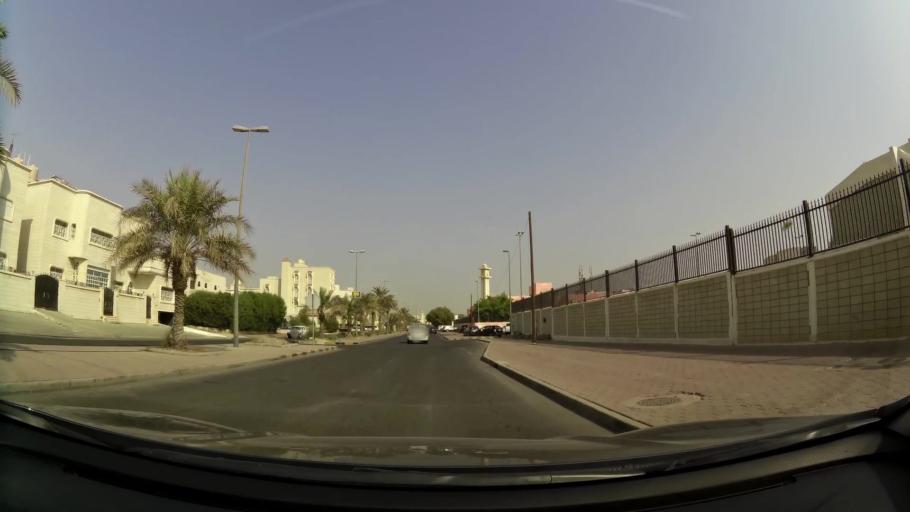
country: KW
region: Al Asimah
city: Ar Rabiyah
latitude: 29.2714
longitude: 47.8699
